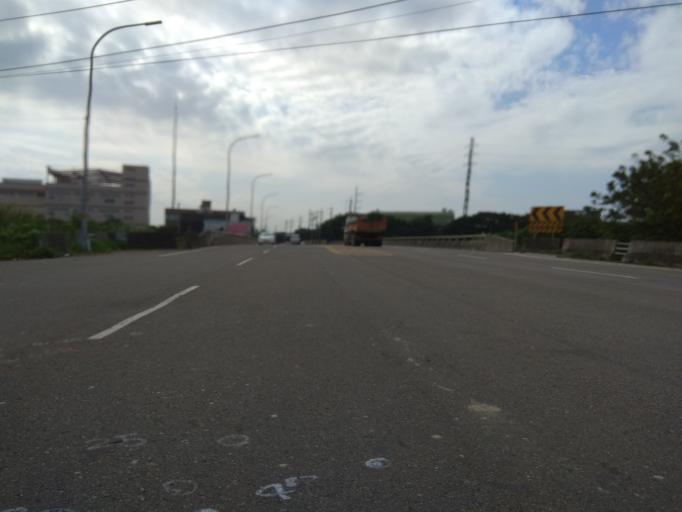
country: TW
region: Taiwan
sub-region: Hsinchu
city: Zhubei
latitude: 24.9844
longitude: 121.0272
